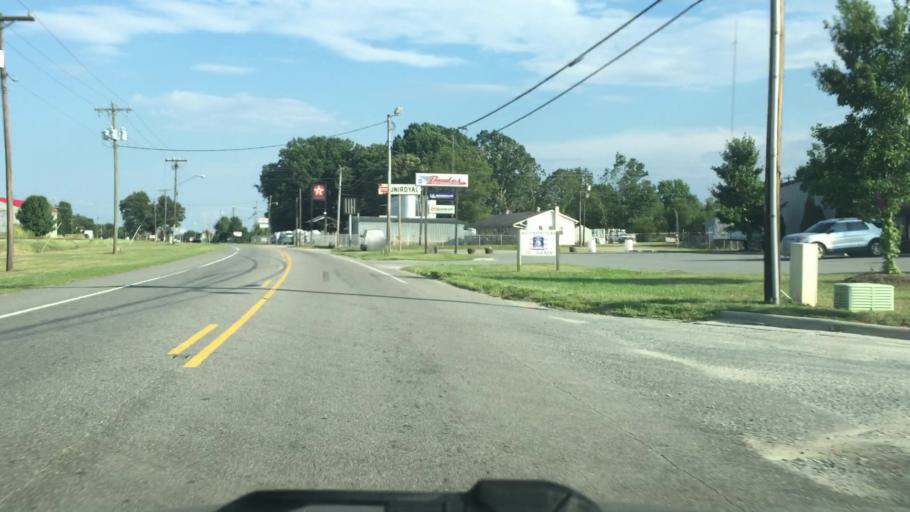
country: US
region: North Carolina
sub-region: Iredell County
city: Mooresville
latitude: 35.6034
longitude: -80.8141
